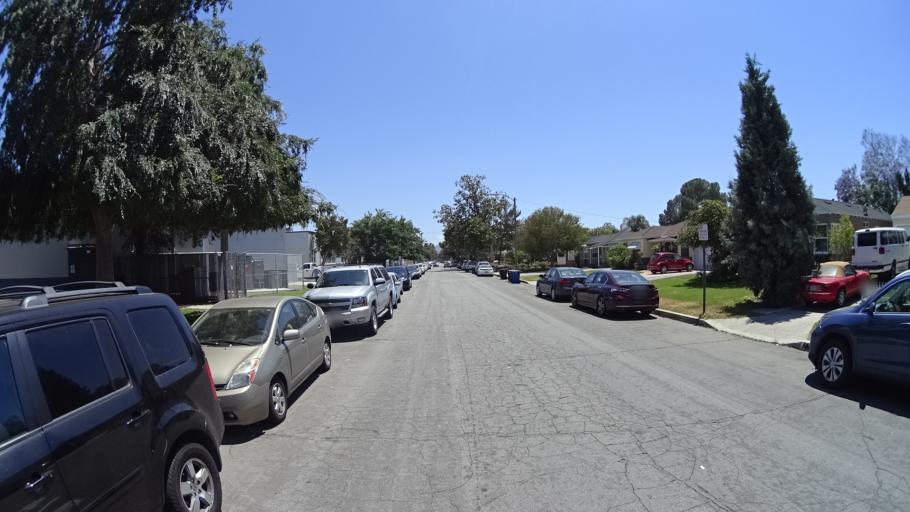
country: US
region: California
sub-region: Los Angeles County
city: North Hollywood
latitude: 34.1809
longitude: -118.3470
